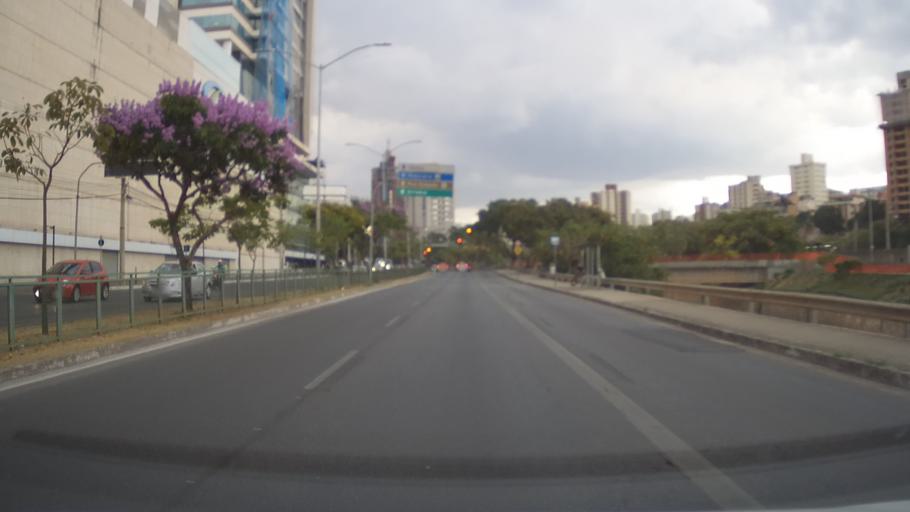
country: BR
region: Minas Gerais
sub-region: Belo Horizonte
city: Belo Horizonte
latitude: -19.9198
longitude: -43.9198
